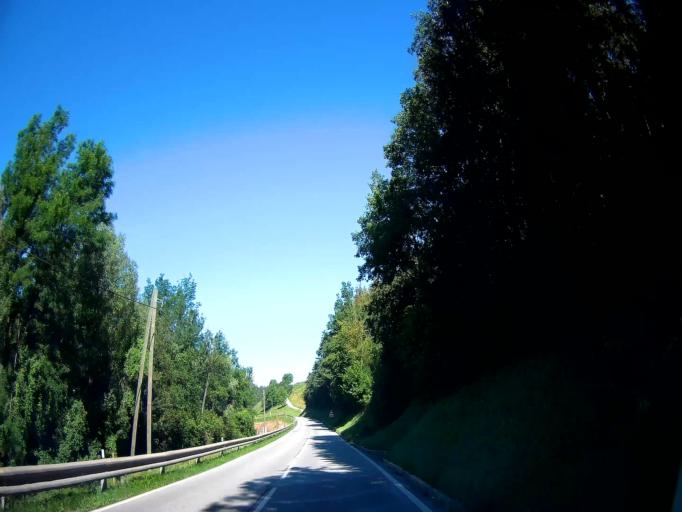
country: AT
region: Carinthia
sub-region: Politischer Bezirk Sankt Veit an der Glan
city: Bruckl
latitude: 46.7531
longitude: 14.5062
